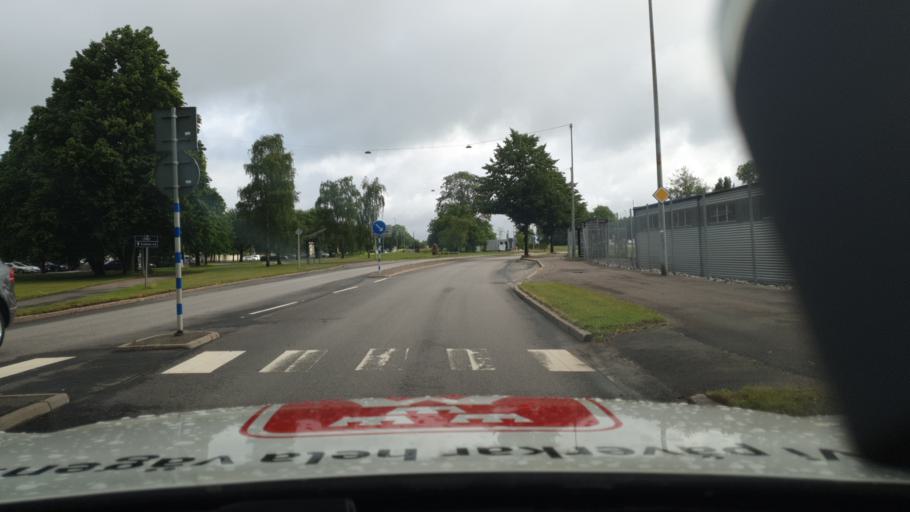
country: SE
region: Vaestra Goetaland
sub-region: Falkopings Kommun
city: Falkoeping
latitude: 58.1872
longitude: 13.5549
